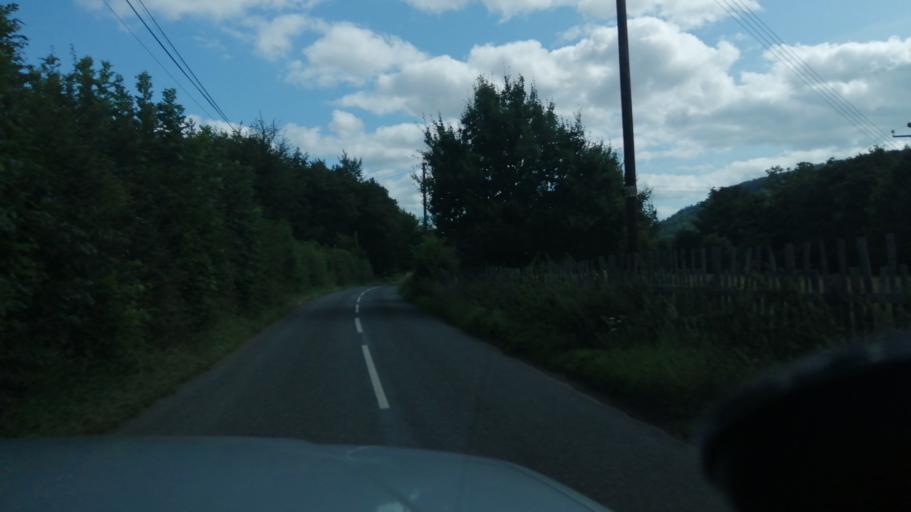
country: GB
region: England
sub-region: Herefordshire
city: Moccas
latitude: 52.0826
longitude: -2.9569
